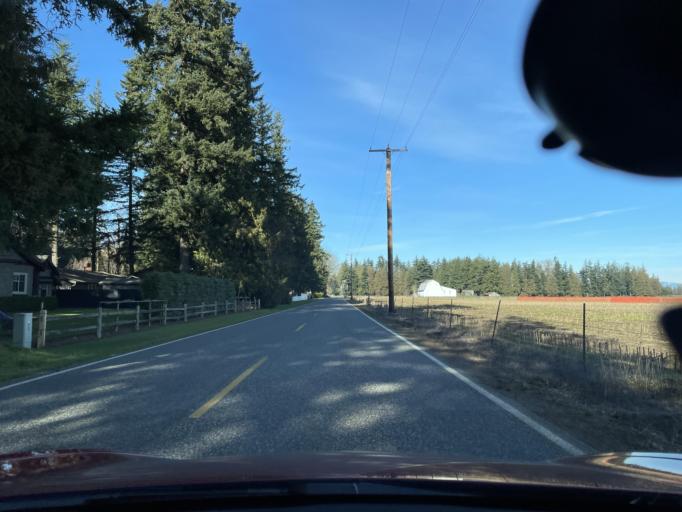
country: US
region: Washington
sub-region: Whatcom County
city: Lynden
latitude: 48.9521
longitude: -122.5073
